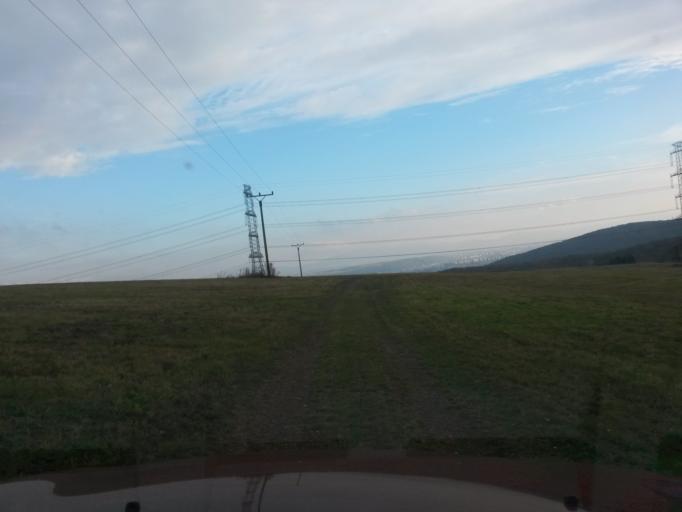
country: SK
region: Kosicky
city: Kosice
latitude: 48.7654
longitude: 21.2152
